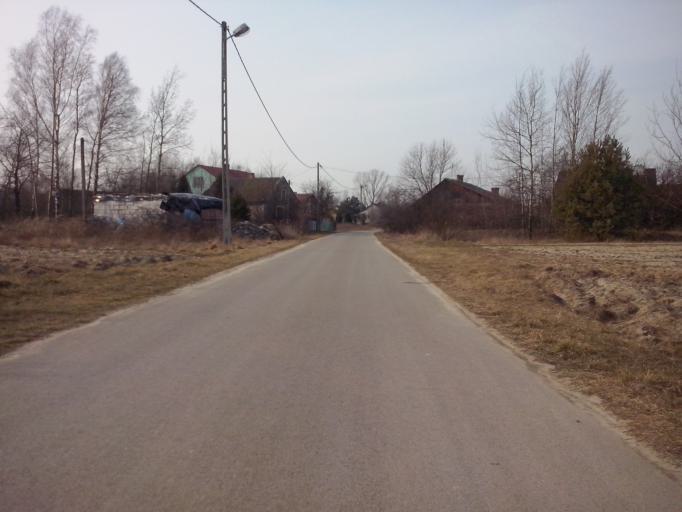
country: PL
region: Subcarpathian Voivodeship
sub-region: Powiat nizanski
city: Krzeszow
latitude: 50.4231
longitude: 22.3647
